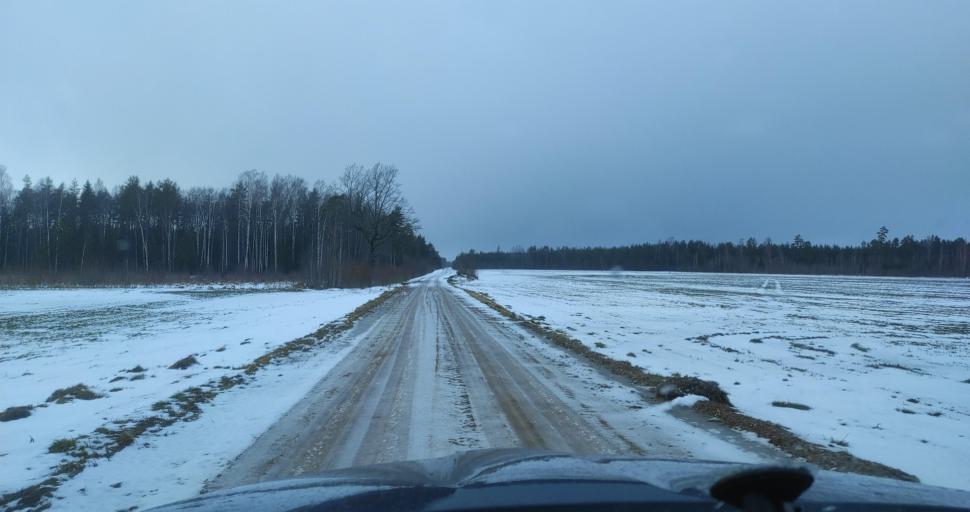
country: LV
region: Dundaga
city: Dundaga
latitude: 57.3758
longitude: 22.1690
